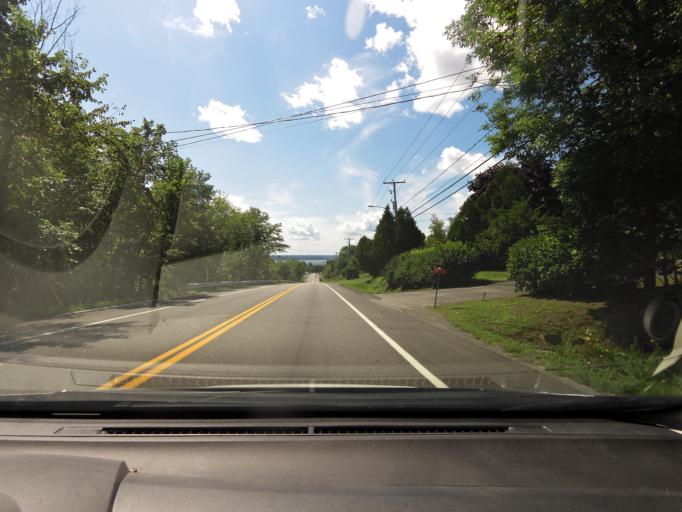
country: CA
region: Quebec
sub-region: Capitale-Nationale
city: Neuville
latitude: 46.7063
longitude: -71.5637
